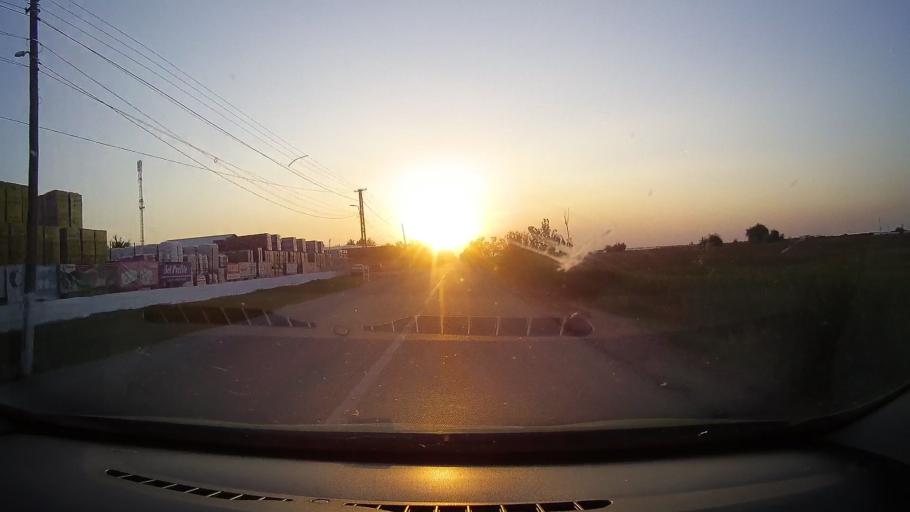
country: RO
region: Arad
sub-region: Comuna Seleus
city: Seleus
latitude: 46.3841
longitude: 21.6951
